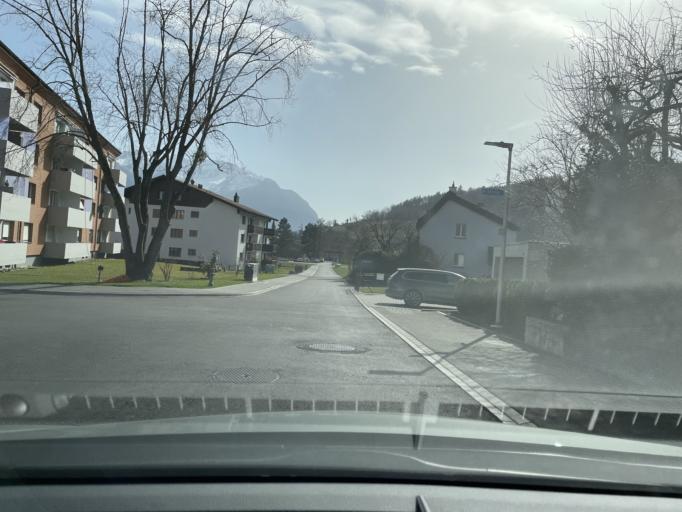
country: CH
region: Saint Gallen
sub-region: Wahlkreis Werdenberg
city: Buchs
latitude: 47.1572
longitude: 9.4742
